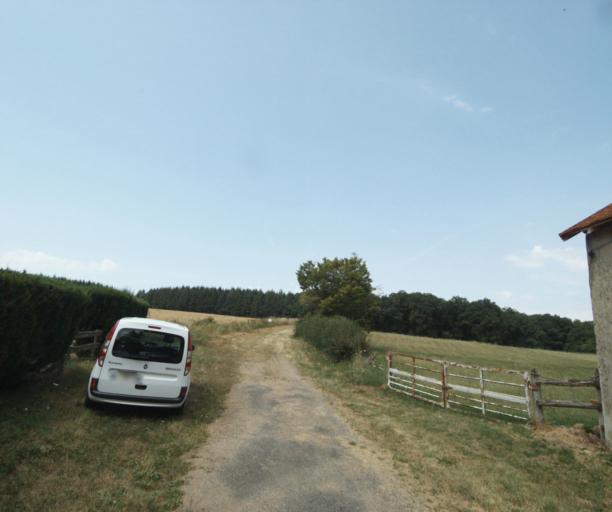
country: FR
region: Bourgogne
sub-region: Departement de Saone-et-Loire
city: Gueugnon
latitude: 46.6068
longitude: 4.0346
